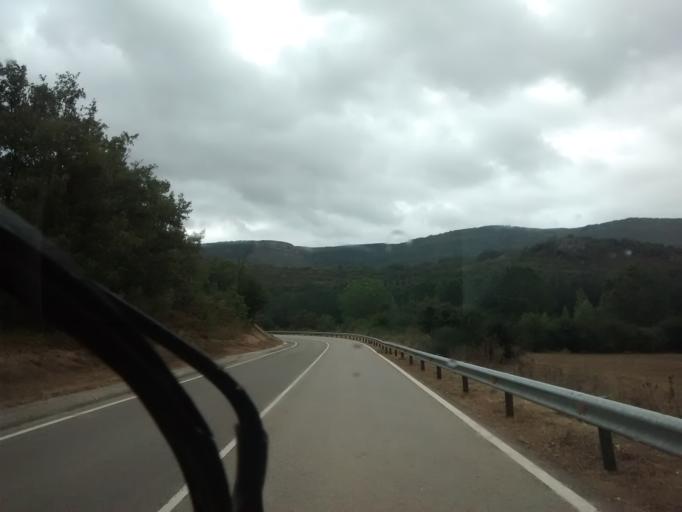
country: ES
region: Castille and Leon
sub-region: Provincia de Palencia
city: Berzosilla
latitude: 42.7894
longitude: -3.9949
